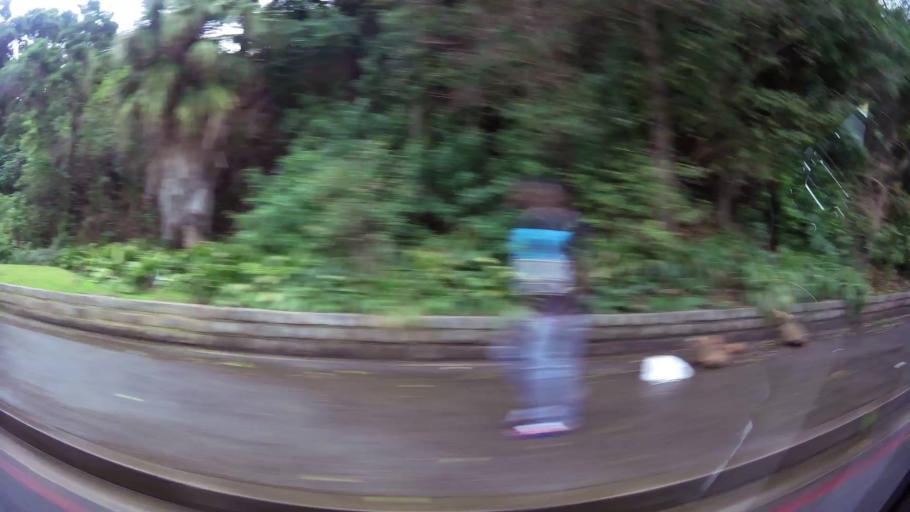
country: ZA
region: Eastern Cape
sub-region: Nelson Mandela Bay Metropolitan Municipality
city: Port Elizabeth
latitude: -33.9593
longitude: 25.6175
